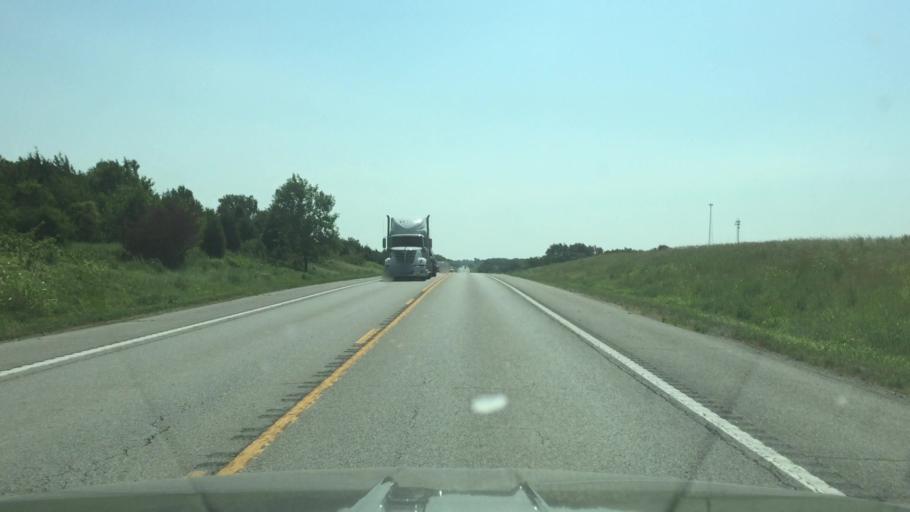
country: US
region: Missouri
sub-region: Pettis County
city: Sedalia
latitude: 38.6942
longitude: -93.1113
